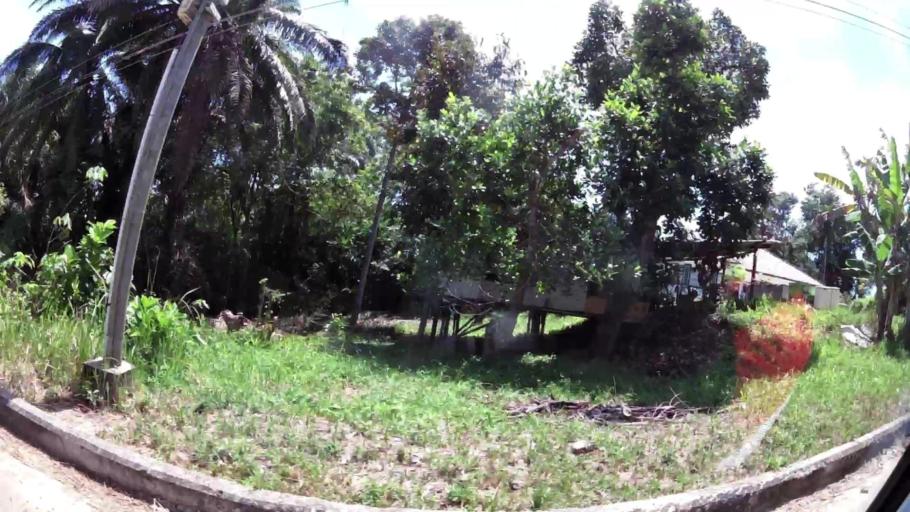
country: BN
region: Brunei and Muara
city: Bandar Seri Begawan
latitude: 4.9326
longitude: 114.9565
